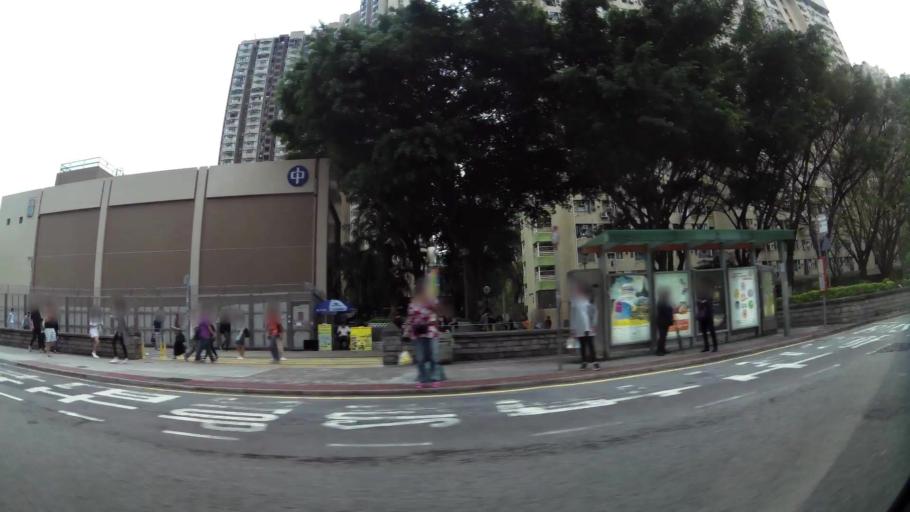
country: HK
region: Tai Po
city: Tai Po
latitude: 22.4523
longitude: 114.1633
